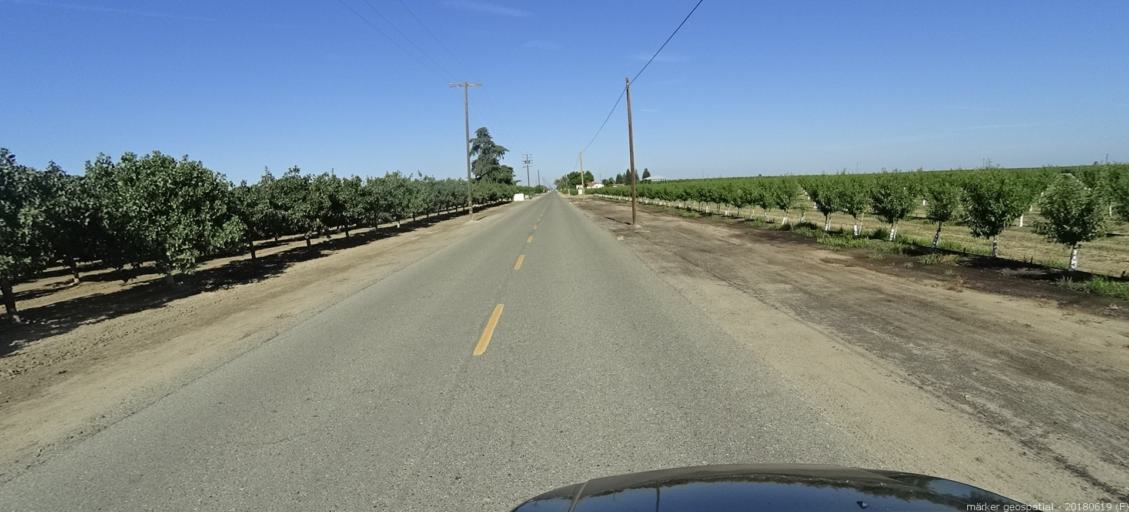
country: US
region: California
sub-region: Fresno County
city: Biola
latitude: 36.8296
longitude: -120.0703
